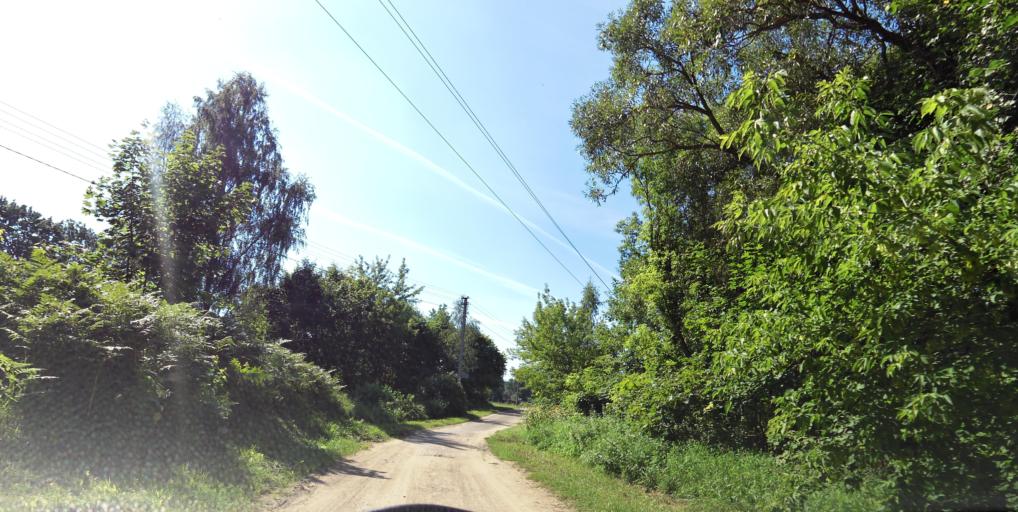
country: LT
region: Vilnius County
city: Rasos
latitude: 54.6803
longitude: 25.3579
